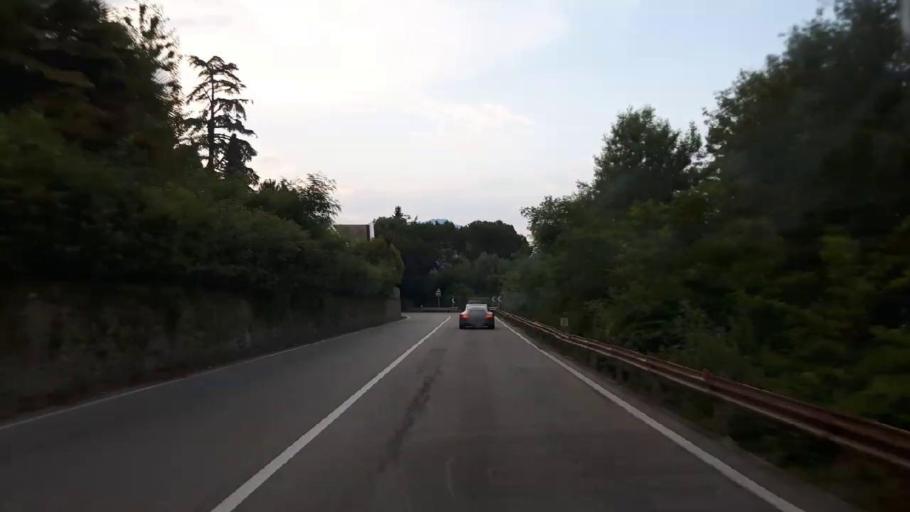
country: IT
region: Piedmont
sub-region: Provincia di Novara
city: Meina
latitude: 45.7826
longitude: 8.5417
